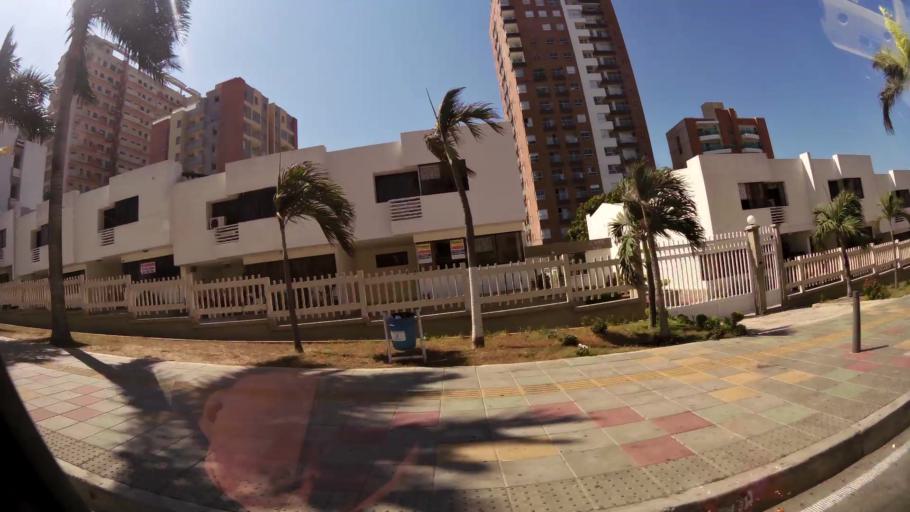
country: CO
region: Atlantico
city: Barranquilla
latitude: 11.0108
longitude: -74.8281
